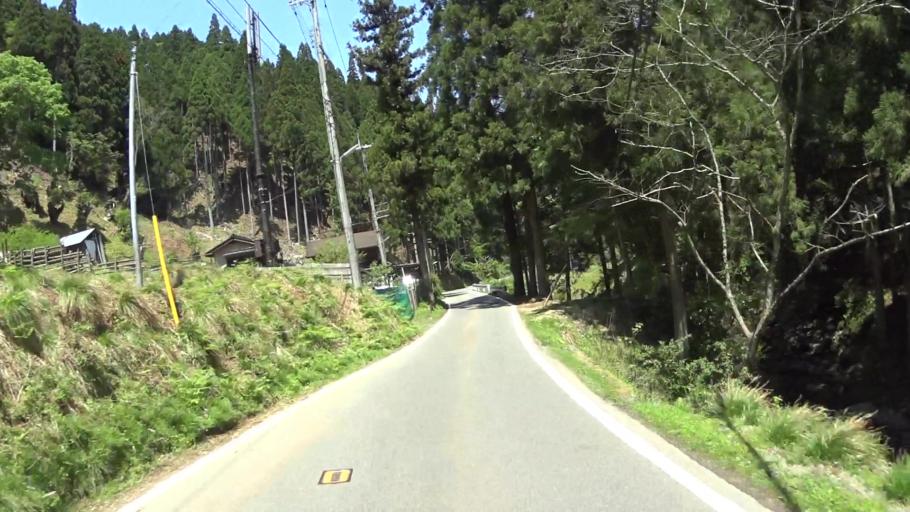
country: JP
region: Shiga Prefecture
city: Kitahama
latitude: 35.2051
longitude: 135.7802
